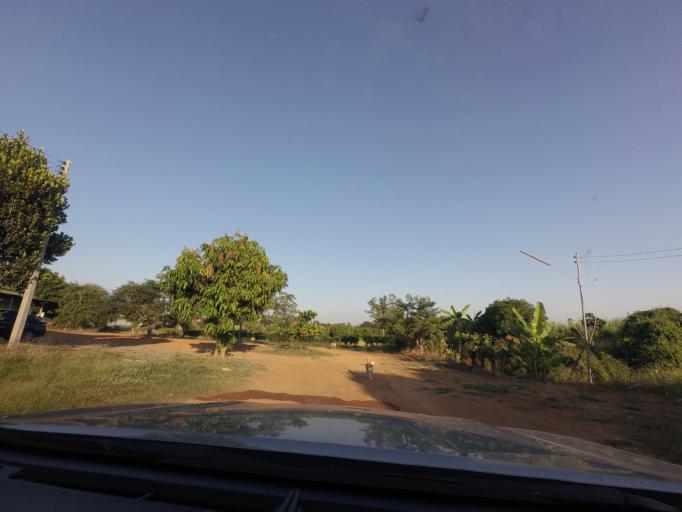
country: TH
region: Sukhothai
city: Sawankhalok
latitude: 17.3943
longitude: 99.7909
